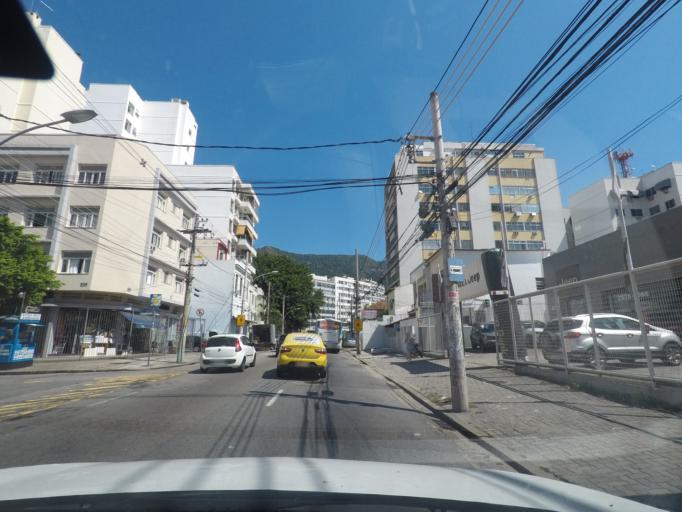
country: BR
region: Rio de Janeiro
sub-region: Rio De Janeiro
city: Rio de Janeiro
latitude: -22.9229
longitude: -43.2368
